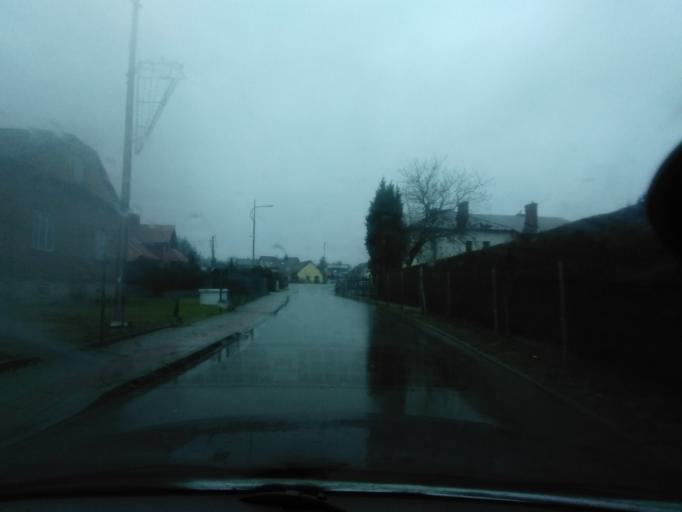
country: PL
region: Subcarpathian Voivodeship
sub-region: Powiat krosnienski
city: Kroscienko Wyzne
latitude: 49.6753
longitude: 21.8321
